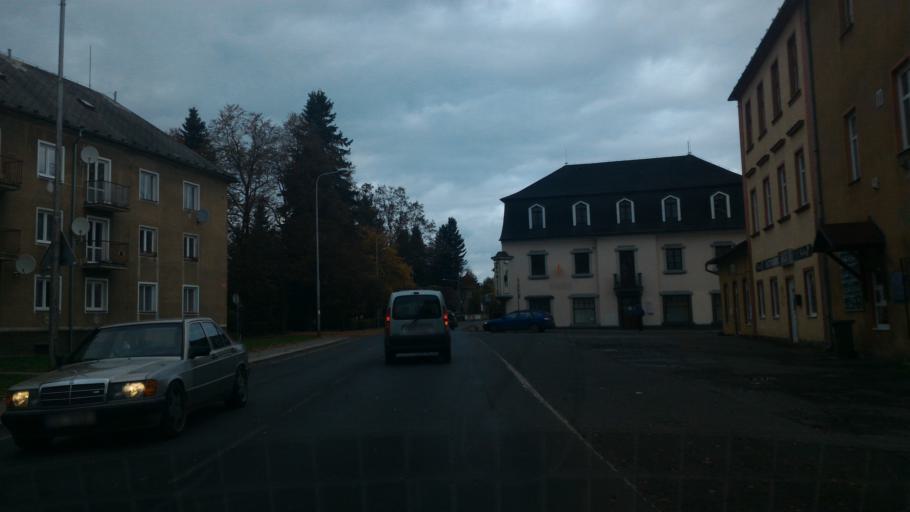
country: CZ
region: Ustecky
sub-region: Okres Decin
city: Rumburk
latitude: 50.9542
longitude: 14.5558
